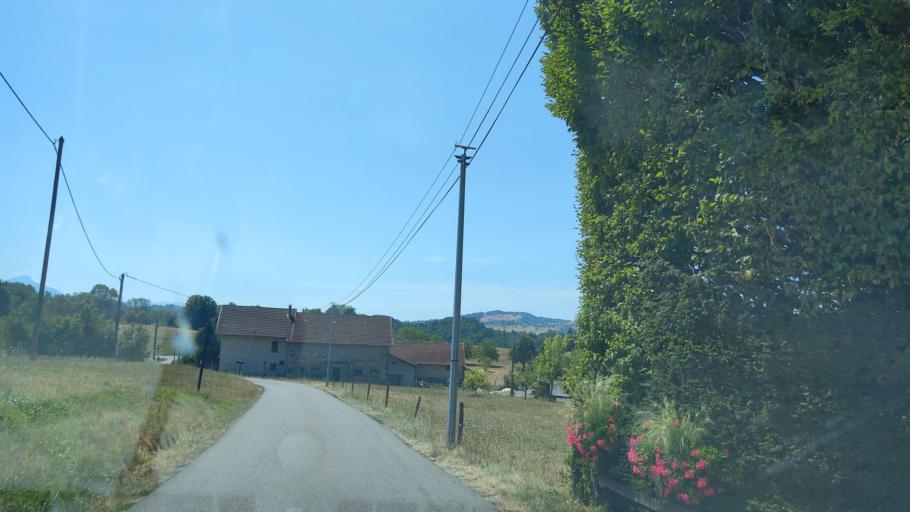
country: FR
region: Rhone-Alpes
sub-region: Departement de la Savoie
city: Novalaise
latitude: 45.5927
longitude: 5.7906
